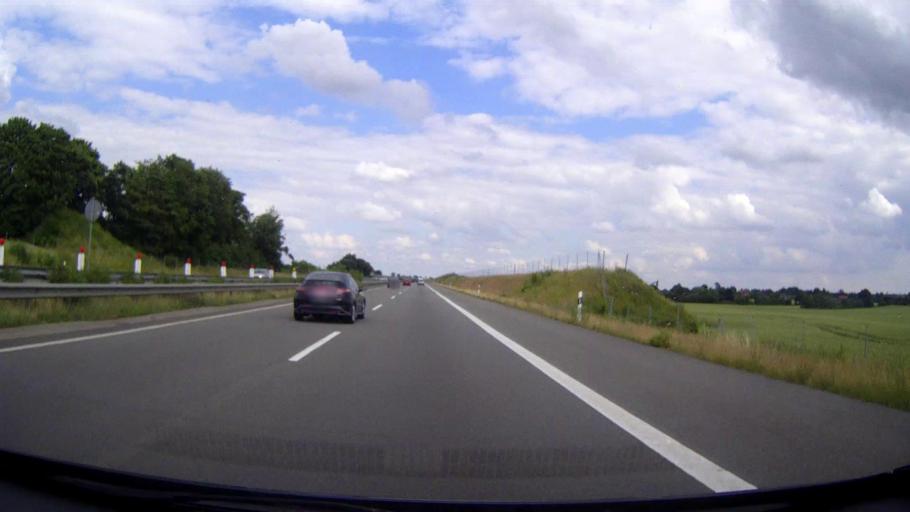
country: DE
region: Schleswig-Holstein
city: Klein Gladebrugge
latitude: 53.9201
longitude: 10.3489
